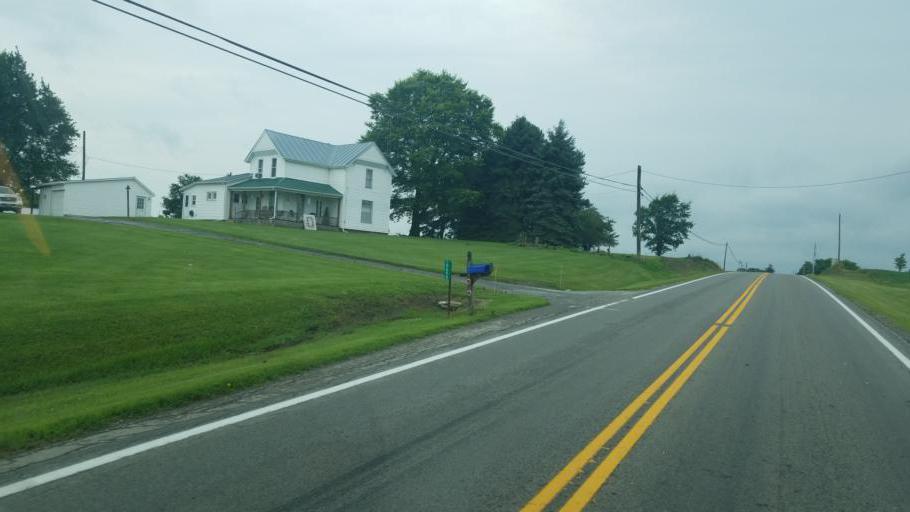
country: US
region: Ohio
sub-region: Hardin County
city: Kenton
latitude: 40.6115
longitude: -83.6803
